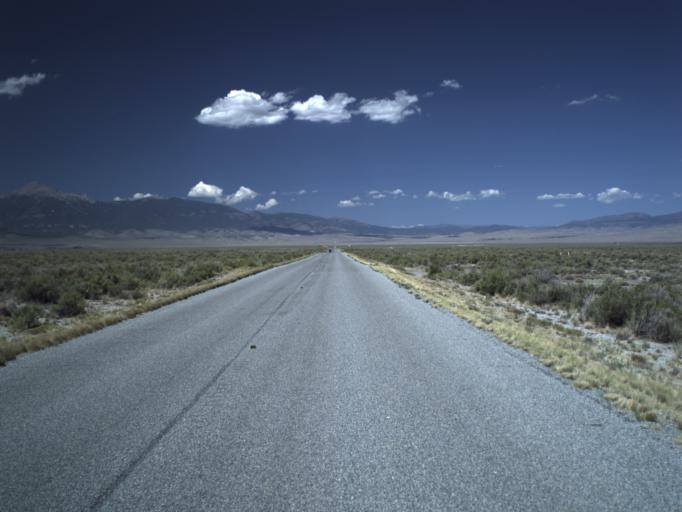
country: US
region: Nevada
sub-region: White Pine County
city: McGill
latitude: 39.0496
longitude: -113.9509
